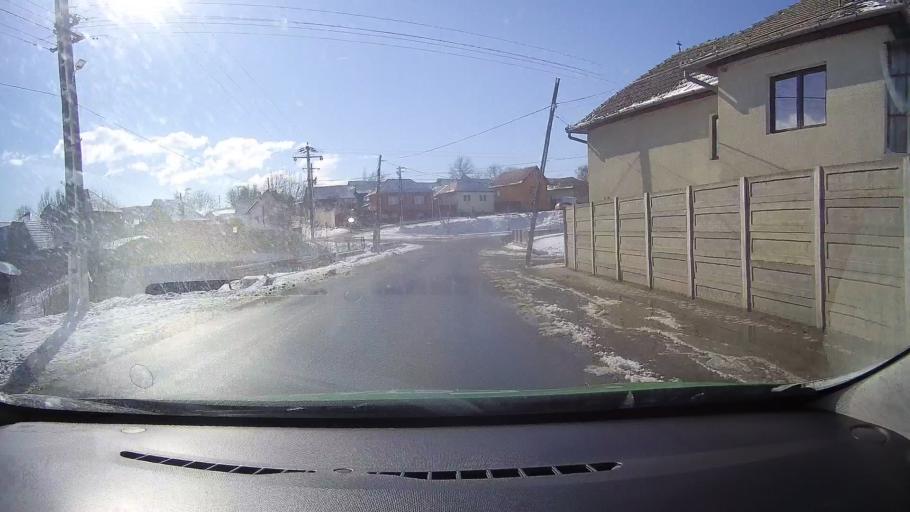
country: RO
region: Sibiu
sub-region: Comuna Rosia
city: Rosia
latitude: 45.8013
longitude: 24.2867
